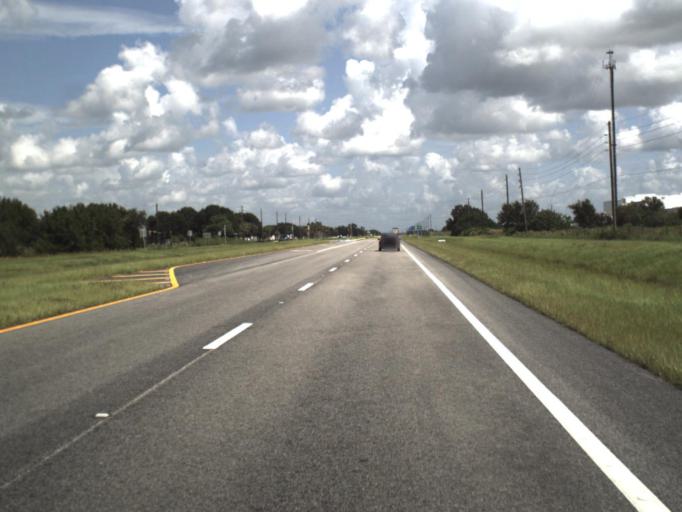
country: US
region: Florida
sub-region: Charlotte County
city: Harbour Heights
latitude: 27.0330
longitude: -81.9583
